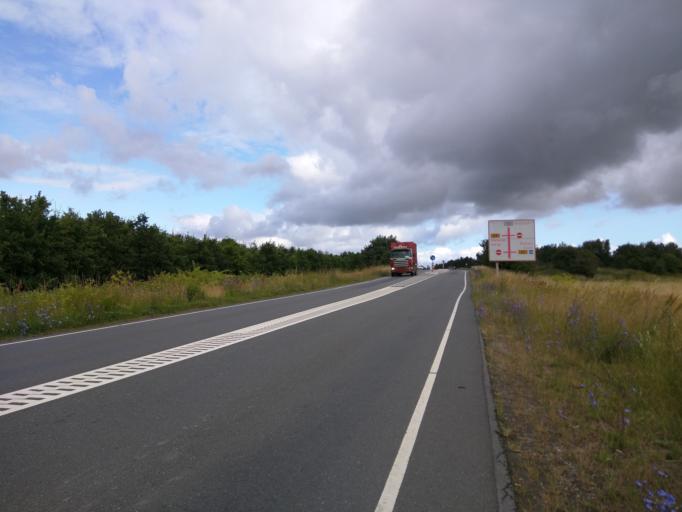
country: DK
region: Zealand
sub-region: Kalundborg Kommune
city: Svebolle
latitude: 55.6670
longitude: 11.2987
